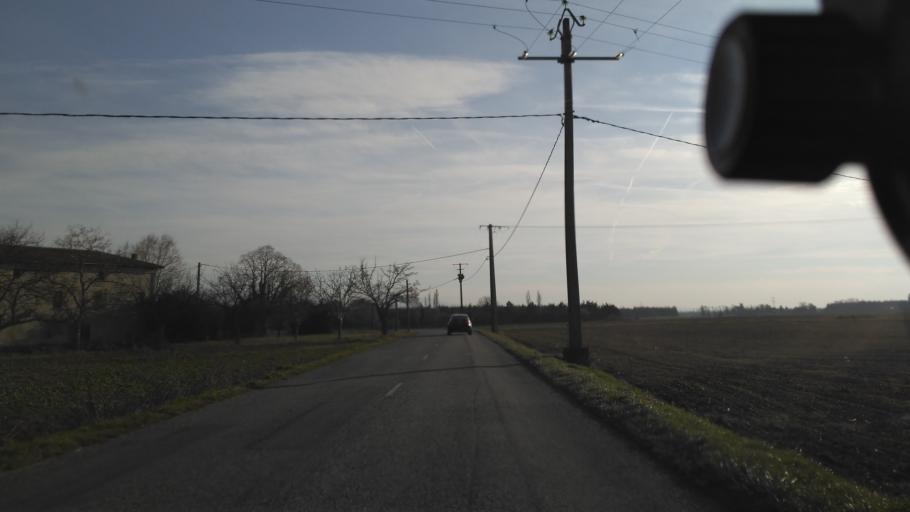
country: FR
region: Rhone-Alpes
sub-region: Departement de la Drome
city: Alixan
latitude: 44.9931
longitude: 5.0036
